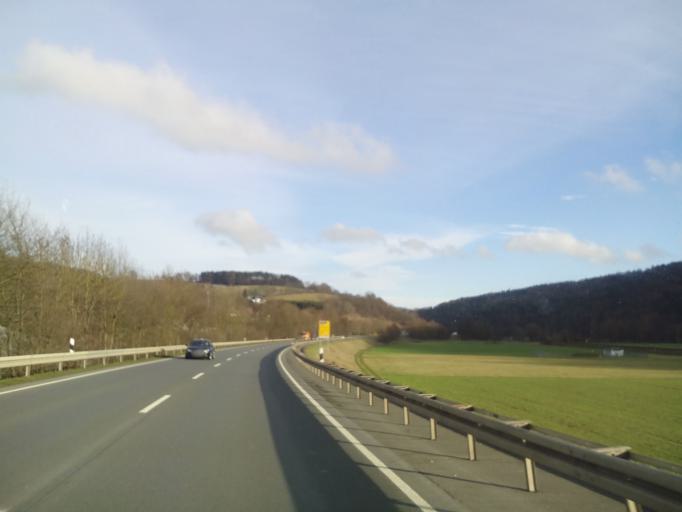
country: DE
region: Bavaria
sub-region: Upper Franconia
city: Kulmbach
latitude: 50.1135
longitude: 11.4734
